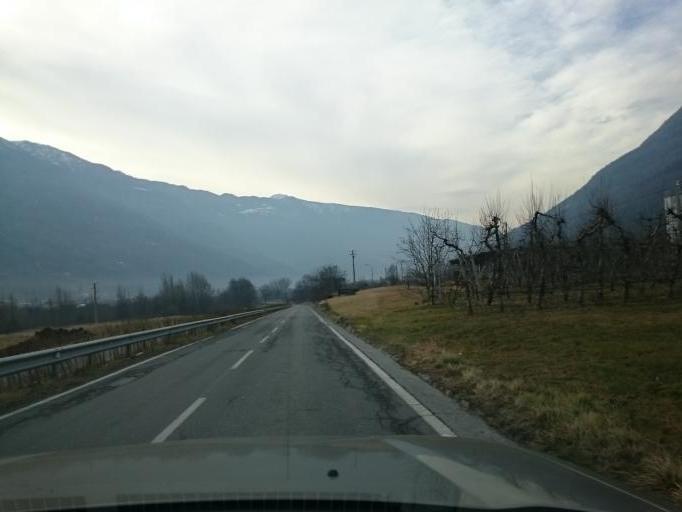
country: IT
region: Lombardy
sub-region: Provincia di Sondrio
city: Mazzo di Valtellina
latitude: 46.2684
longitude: 10.2539
